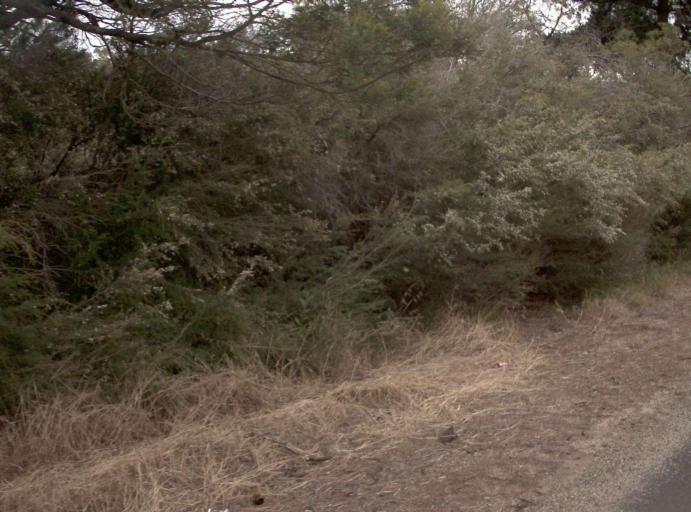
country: AU
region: Victoria
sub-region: Wellington
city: Sale
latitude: -38.2075
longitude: 147.0693
